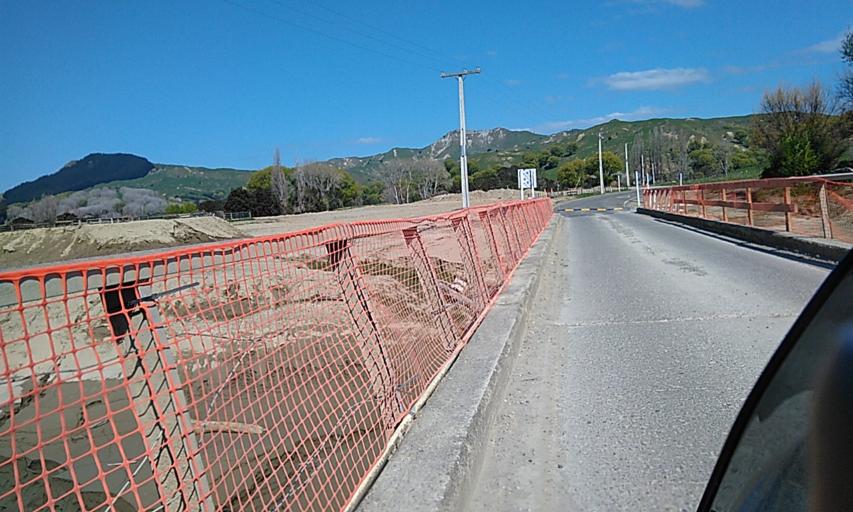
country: NZ
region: Gisborne
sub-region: Gisborne District
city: Gisborne
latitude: -38.3545
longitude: 178.1980
